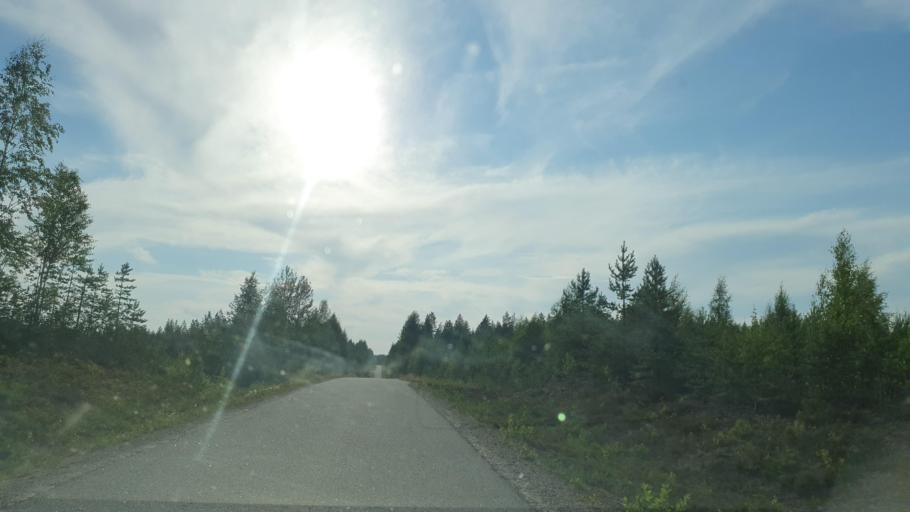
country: FI
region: Kainuu
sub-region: Kehys-Kainuu
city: Kuhmo
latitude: 64.2801
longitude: 29.4194
